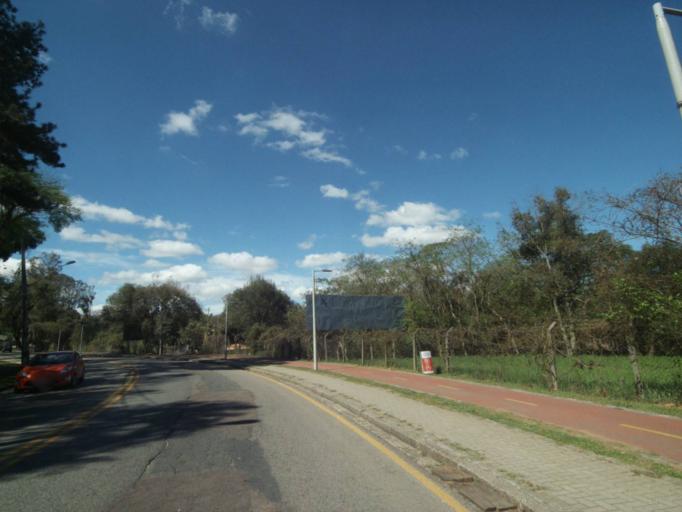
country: BR
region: Parana
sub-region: Curitiba
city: Curitiba
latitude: -25.3940
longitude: -49.2701
